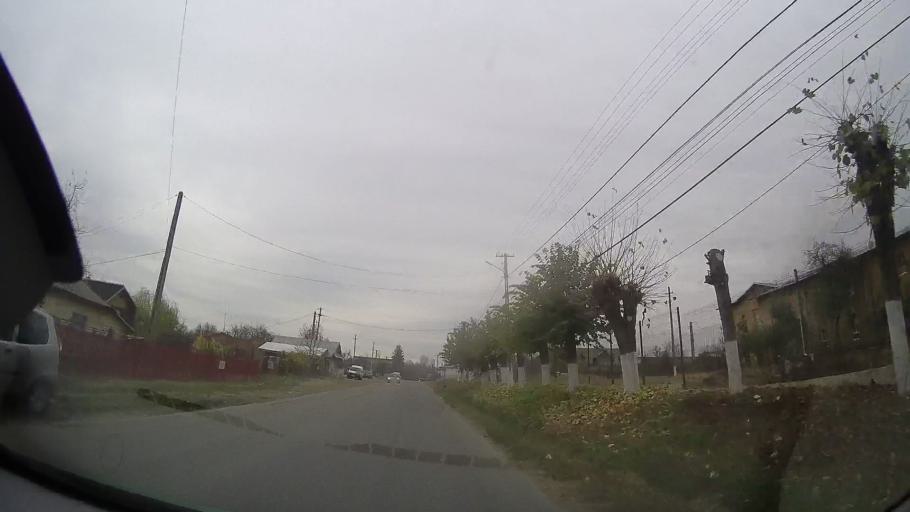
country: RO
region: Prahova
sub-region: Oras Urlati
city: Urlati
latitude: 45.0130
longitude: 26.2285
